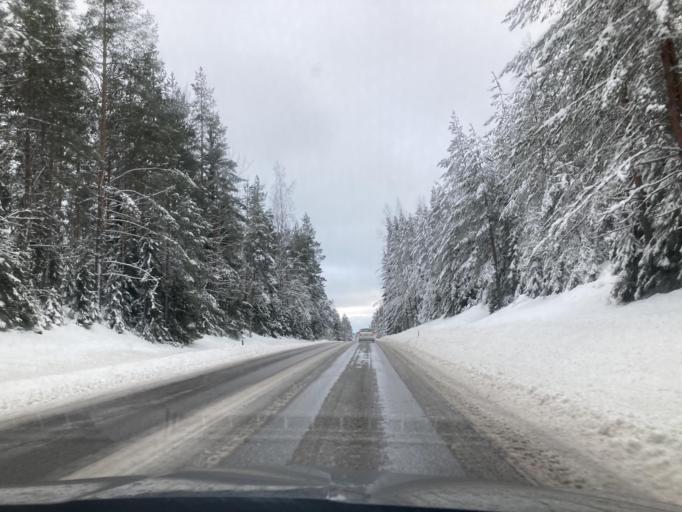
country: FI
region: Paijanne Tavastia
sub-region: Lahti
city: Padasjoki
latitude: 61.3674
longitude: 25.2163
